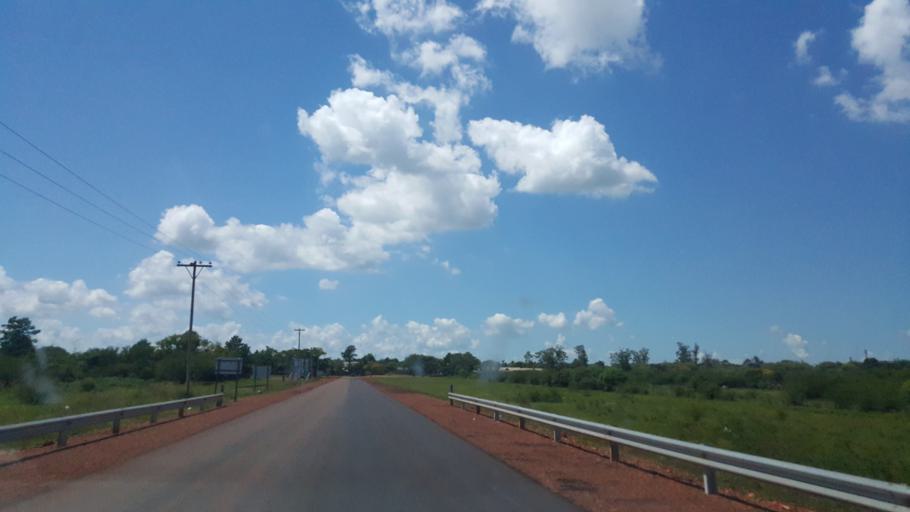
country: AR
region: Corrientes
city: Santo Tome
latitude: -28.5404
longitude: -56.0501
